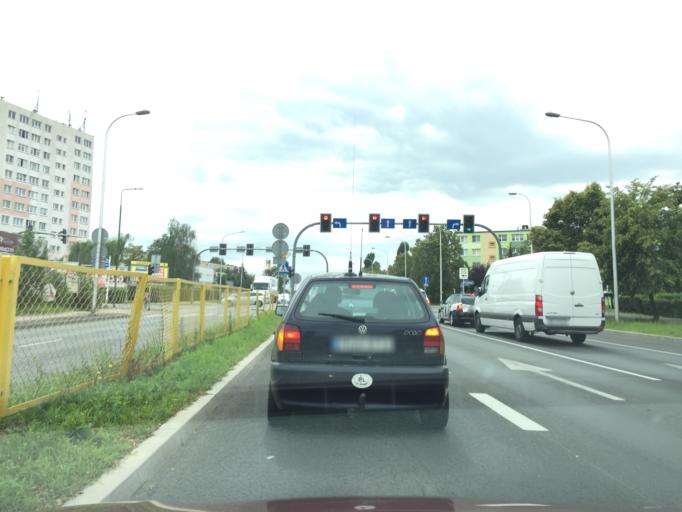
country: PL
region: Greater Poland Voivodeship
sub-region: Kalisz
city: Kalisz
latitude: 51.7508
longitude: 18.0677
